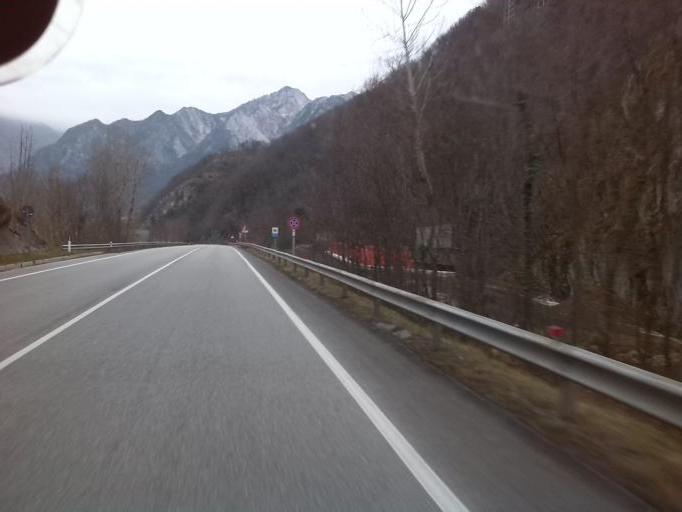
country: IT
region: Friuli Venezia Giulia
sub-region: Provincia di Udine
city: Bordano
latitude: 46.3057
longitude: 13.1239
